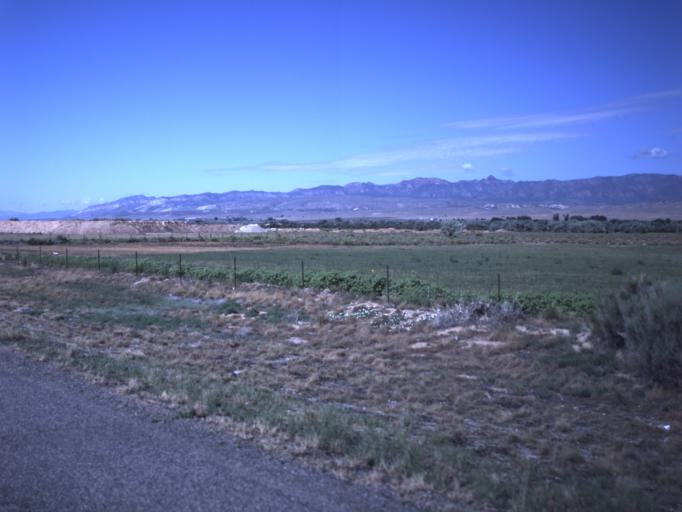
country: US
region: Utah
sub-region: Sevier County
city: Salina
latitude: 39.0008
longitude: -111.8410
